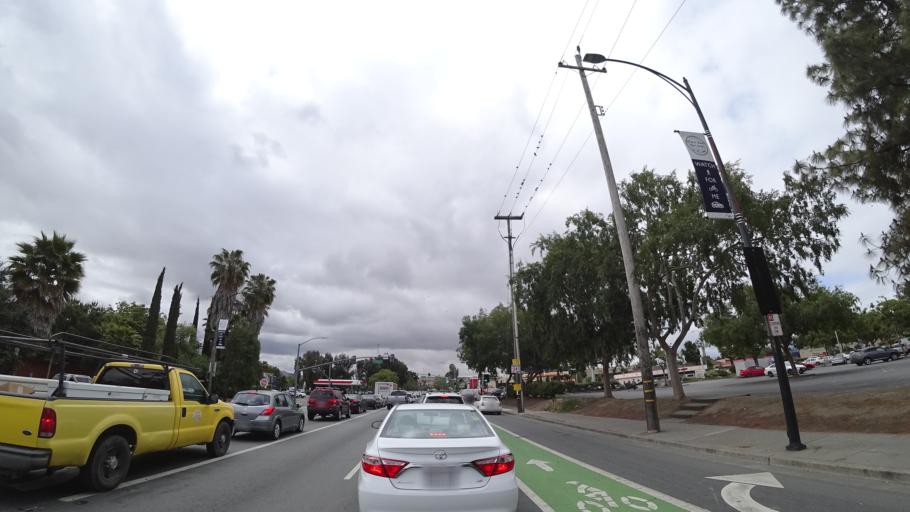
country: US
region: California
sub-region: Santa Clara County
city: Seven Trees
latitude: 37.3230
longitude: -121.8266
